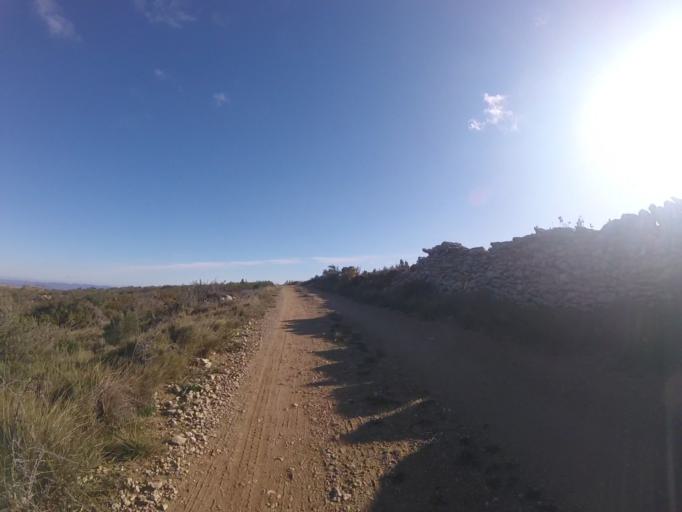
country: ES
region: Valencia
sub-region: Provincia de Castello
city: Sarratella
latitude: 40.3010
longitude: 0.0325
